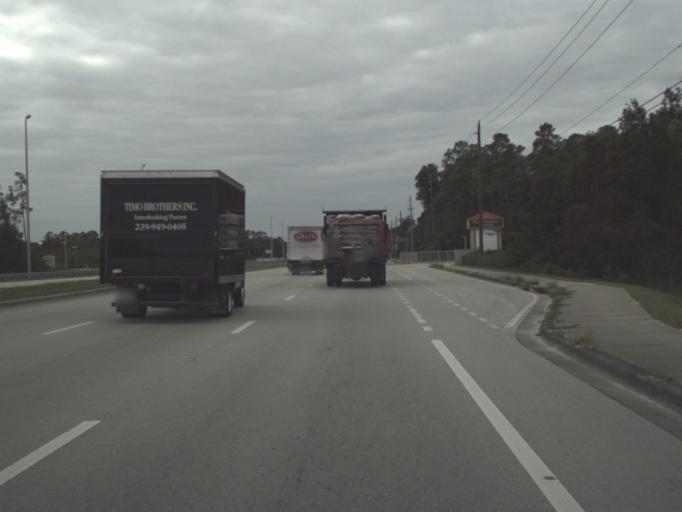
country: US
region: Florida
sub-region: Collier County
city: Lely Resort
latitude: 26.1088
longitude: -81.6873
